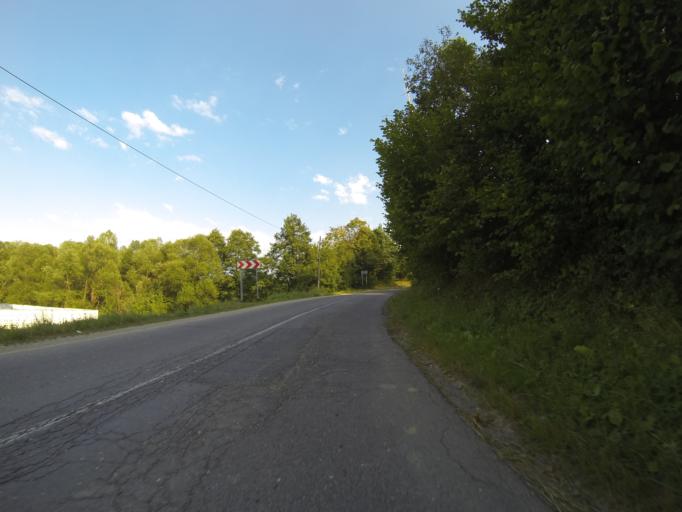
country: RO
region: Brasov
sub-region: Comuna Sinca Noua
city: Sinca Noua
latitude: 45.7295
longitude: 25.2354
